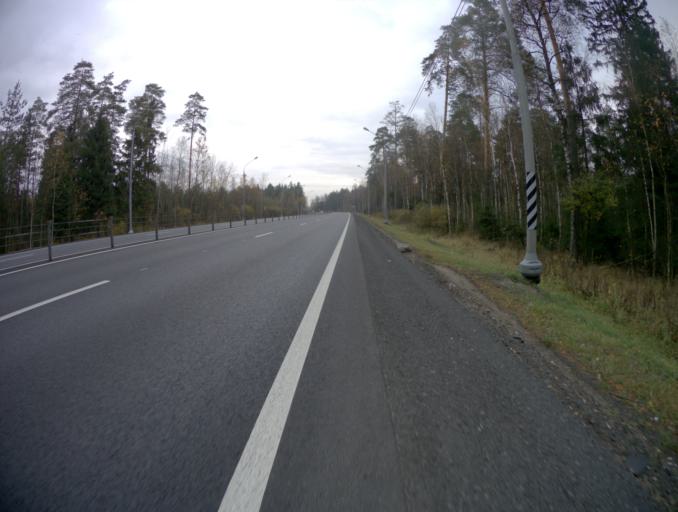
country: RU
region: Moskovskaya
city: Malaya Dubna
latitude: 55.8657
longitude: 38.9634
